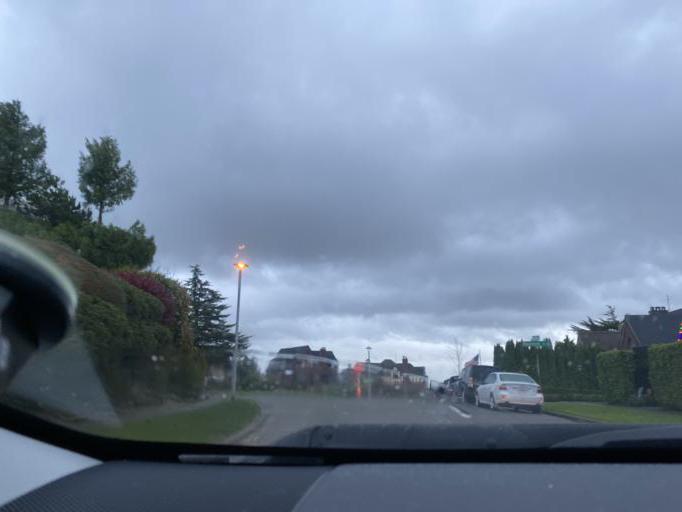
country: US
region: Washington
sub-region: King County
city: Seattle
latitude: 47.6397
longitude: -122.4071
